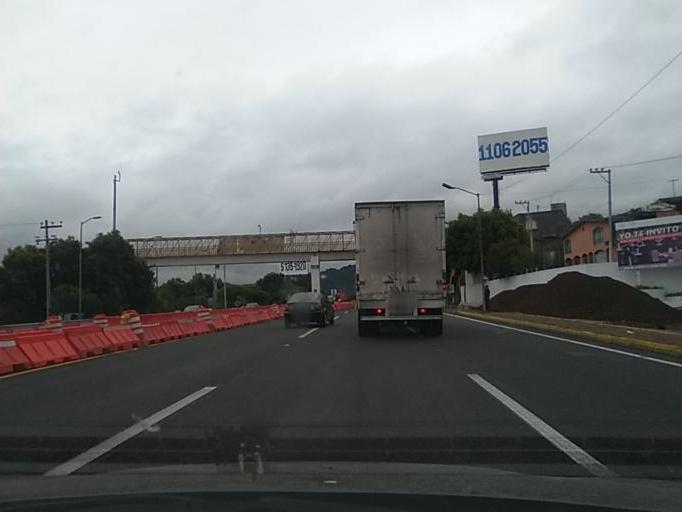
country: MX
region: Mexico City
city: Xochimilco
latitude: 19.2406
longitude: -99.1478
